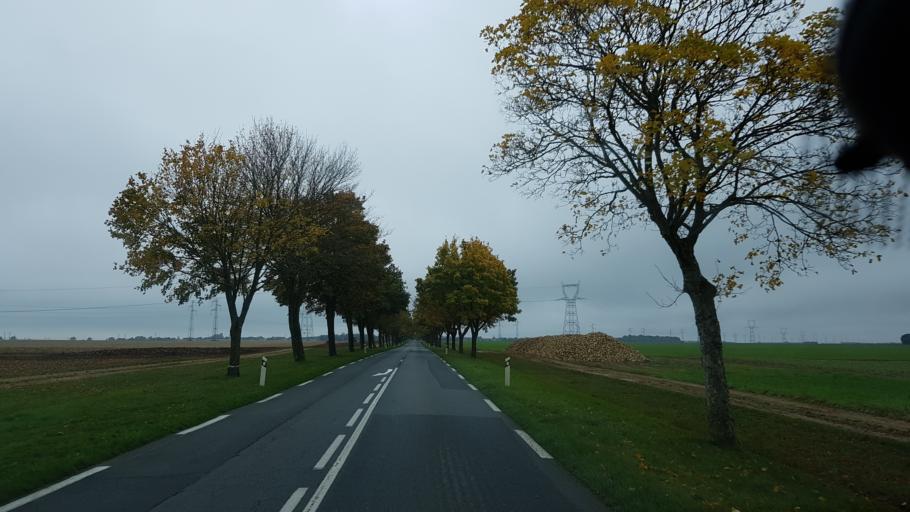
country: FR
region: Ile-de-France
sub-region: Departement de l'Essonne
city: Pussay
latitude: 48.3383
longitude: 1.9902
